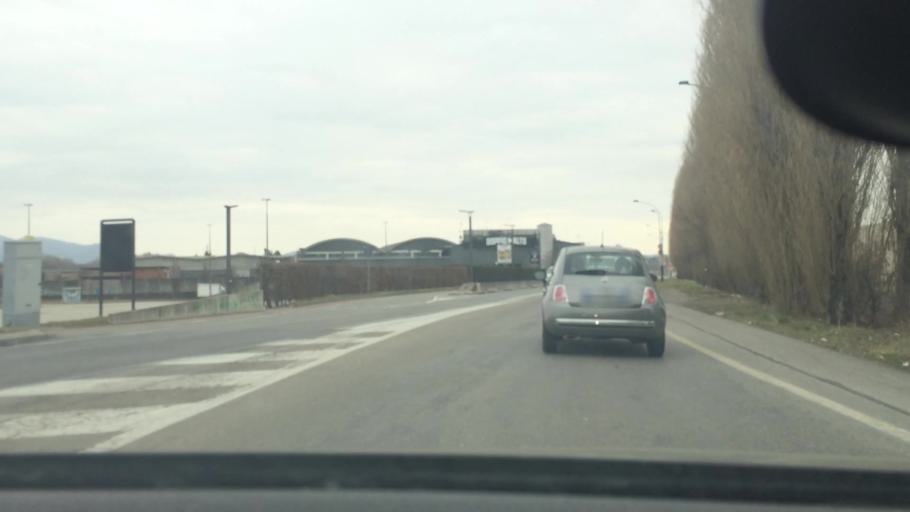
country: IT
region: Lombardy
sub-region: Provincia di Como
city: Erba
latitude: 45.8014
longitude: 9.2373
